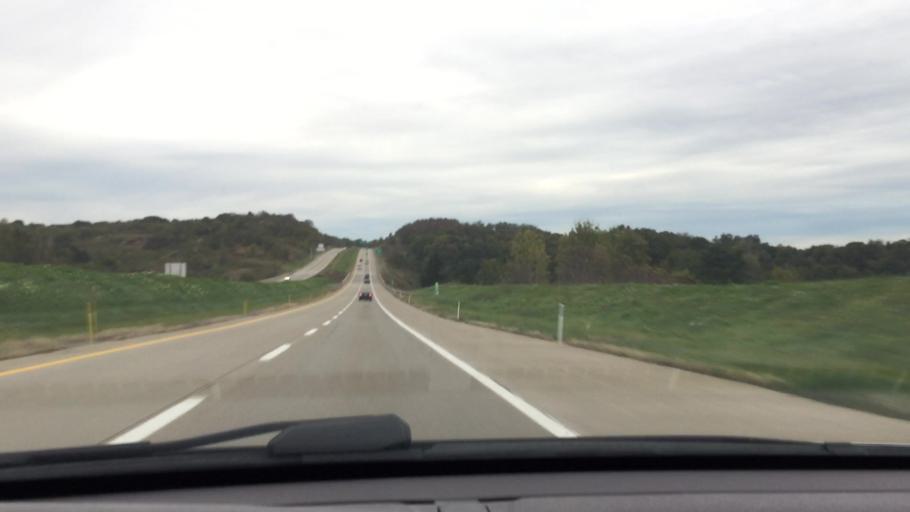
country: US
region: Pennsylvania
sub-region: Lawrence County
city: Oakland
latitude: 40.9542
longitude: -80.3936
